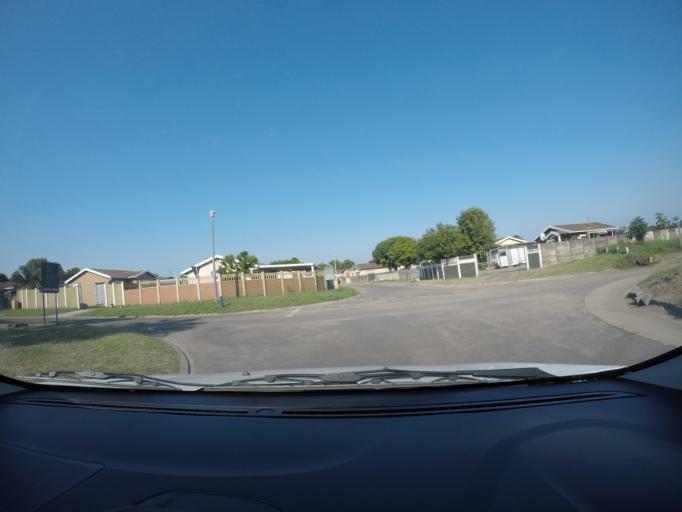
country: ZA
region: KwaZulu-Natal
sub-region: uThungulu District Municipality
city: Richards Bay
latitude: -28.7174
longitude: 32.0361
